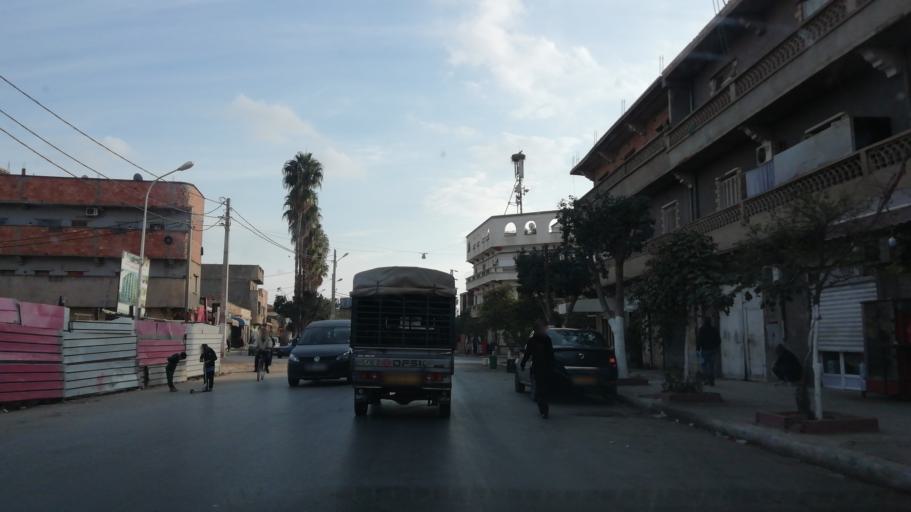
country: DZ
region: Mascara
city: Mascara
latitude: 35.5949
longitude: 0.0644
